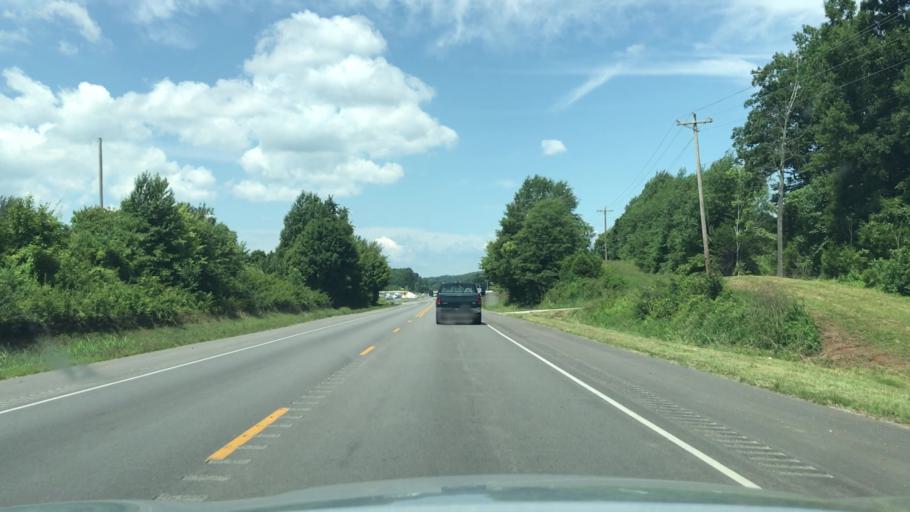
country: US
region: Kentucky
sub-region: Clinton County
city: Albany
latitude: 36.7542
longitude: -85.1308
